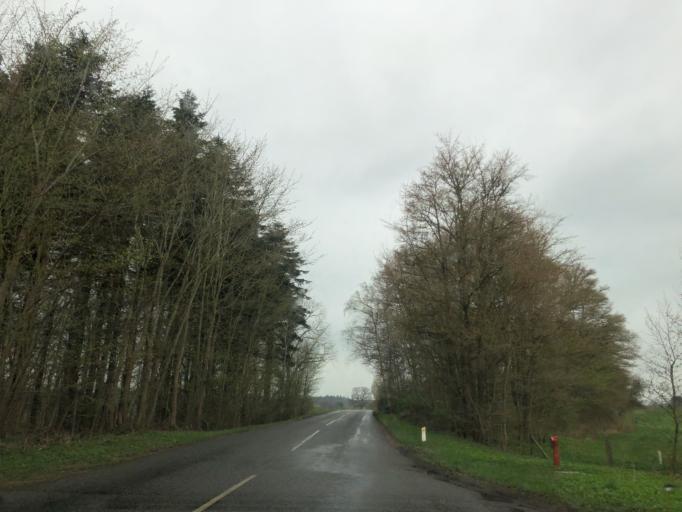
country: DK
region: Zealand
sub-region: Lejre Kommune
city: Kirke Hvalso
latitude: 55.5280
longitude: 11.8579
